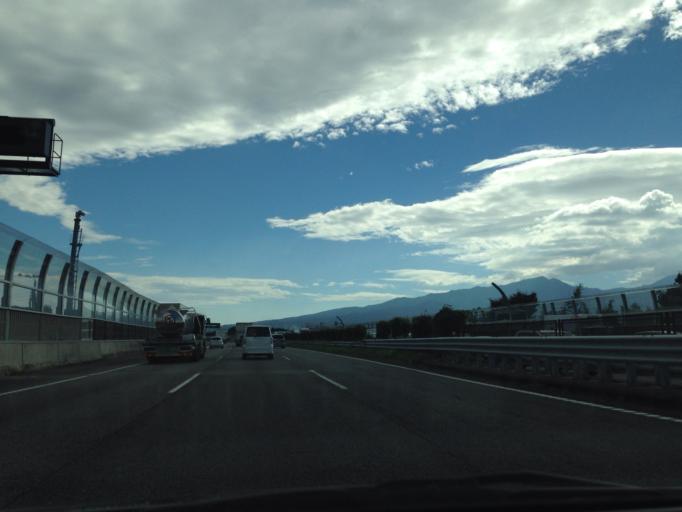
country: JP
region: Shizuoka
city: Gotemba
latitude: 35.2801
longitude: 138.9213
